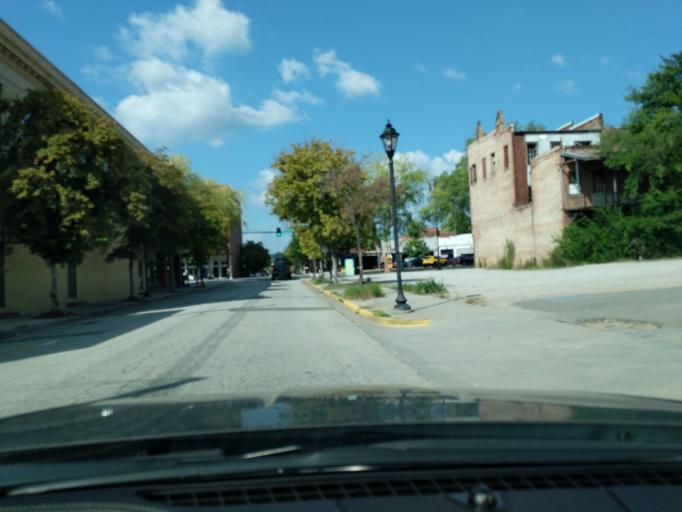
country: US
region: Georgia
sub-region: Richmond County
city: Augusta
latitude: 33.4771
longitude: -81.9730
